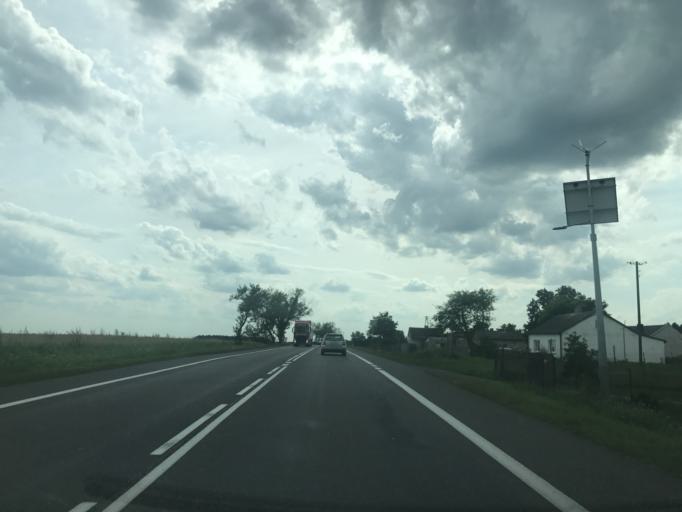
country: PL
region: Masovian Voivodeship
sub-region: Powiat mlawski
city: Strzegowo
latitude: 52.9584
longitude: 20.2991
